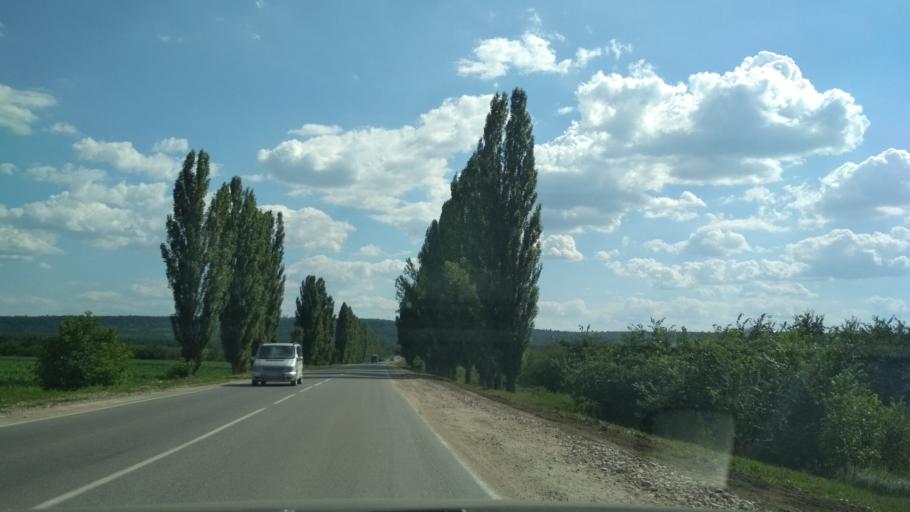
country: MD
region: Chisinau
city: Vadul lui Voda
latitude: 47.1007
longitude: 29.0982
